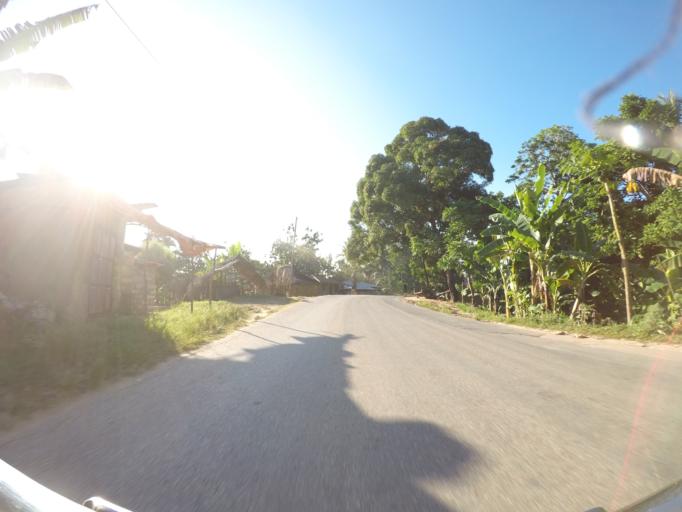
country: TZ
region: Pemba South
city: Chake Chake
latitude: -5.3081
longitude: 39.7468
